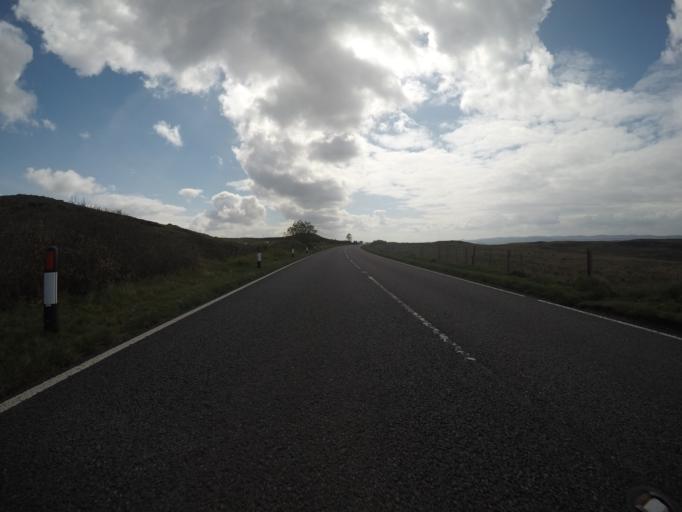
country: GB
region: Scotland
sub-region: Highland
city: Portree
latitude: 57.5568
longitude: -6.3640
